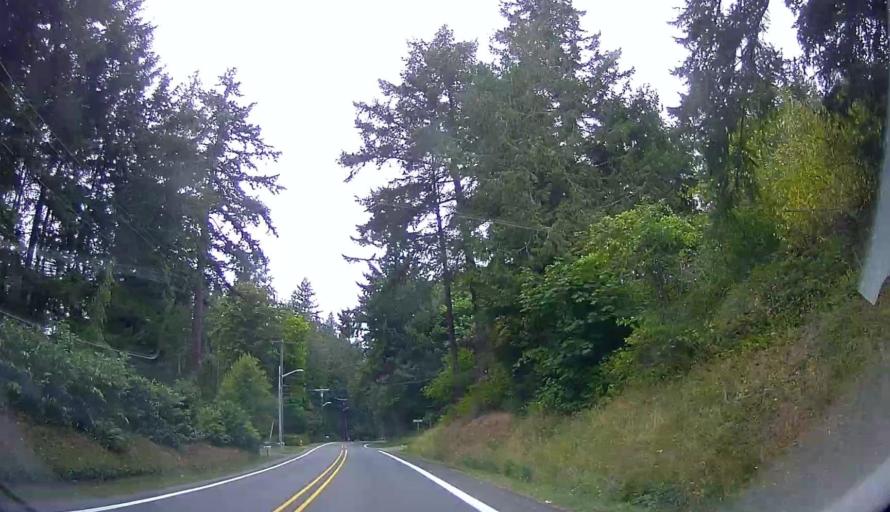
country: US
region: Washington
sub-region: Snohomish County
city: Warm Beach
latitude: 48.1520
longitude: -122.3605
